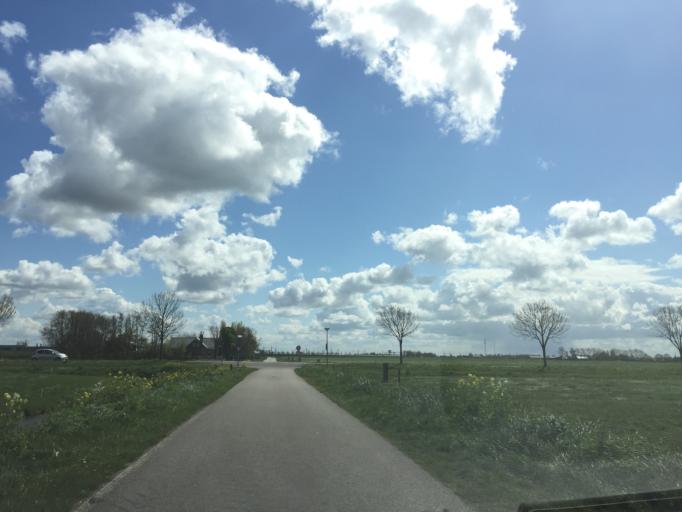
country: NL
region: South Holland
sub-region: Gemeente Kaag en Braassem
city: Oude Wetering
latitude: 52.1988
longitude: 4.6054
